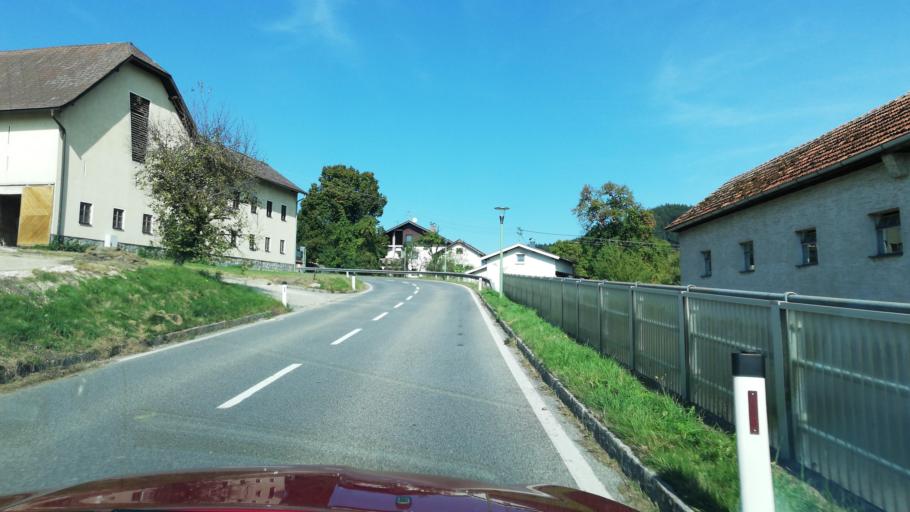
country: AT
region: Upper Austria
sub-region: Politischer Bezirk Vocklabruck
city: Zell am Pettenfirst
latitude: 48.0978
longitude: 13.5706
